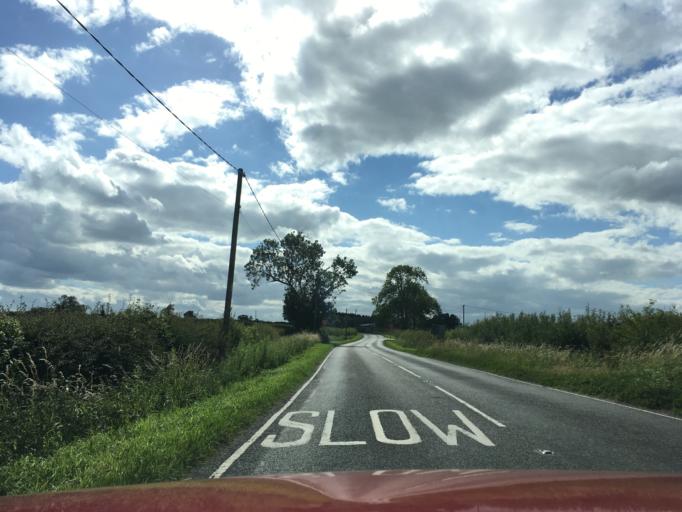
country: GB
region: England
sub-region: Leicestershire
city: Coalville
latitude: 52.7788
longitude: -1.3513
